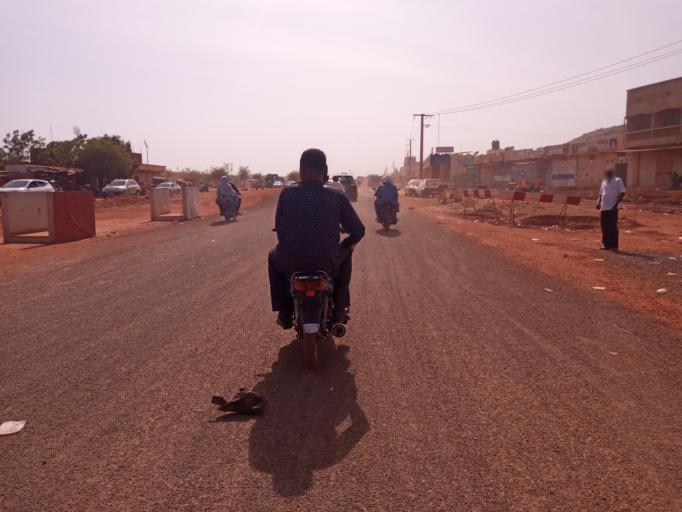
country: ML
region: Bamako
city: Bamako
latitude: 12.6093
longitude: -7.9178
